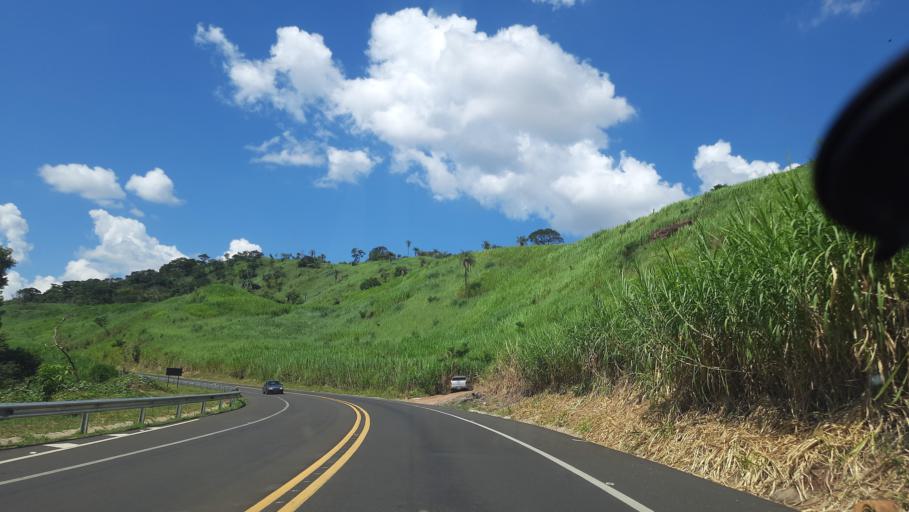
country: BR
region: Sao Paulo
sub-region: Sao Jose Do Rio Pardo
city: Sao Jose do Rio Pardo
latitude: -21.6029
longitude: -46.9404
